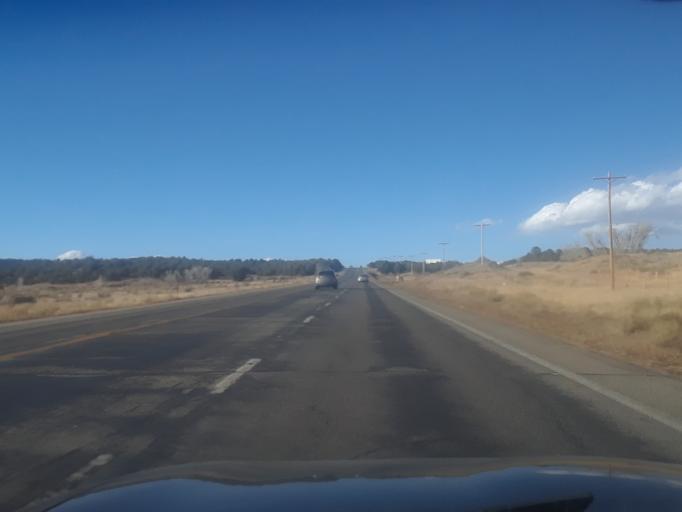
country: US
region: Colorado
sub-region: Chaffee County
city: Salida
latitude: 38.6506
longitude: -106.0848
